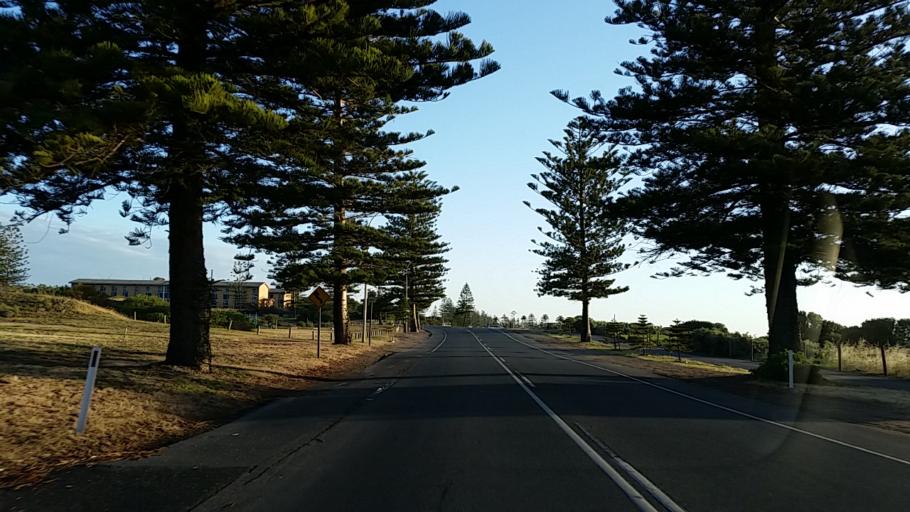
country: AU
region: South Australia
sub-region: Port Adelaide Enfield
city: Birkenhead
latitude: -34.8075
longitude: 138.4914
